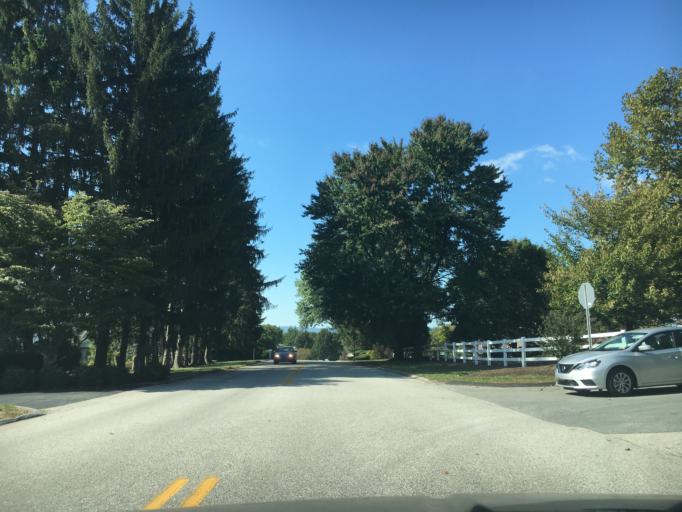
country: US
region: Pennsylvania
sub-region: York County
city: Valley View
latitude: 39.9429
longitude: -76.7111
